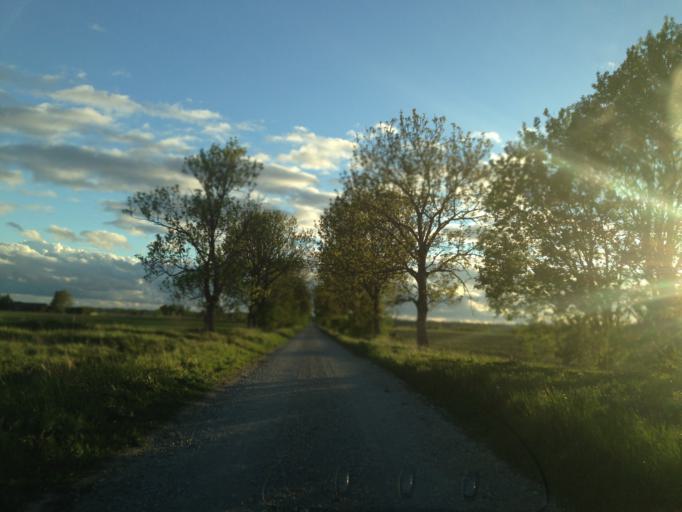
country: EE
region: Raplamaa
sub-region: Maerjamaa vald
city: Marjamaa
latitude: 58.7589
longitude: 24.2039
